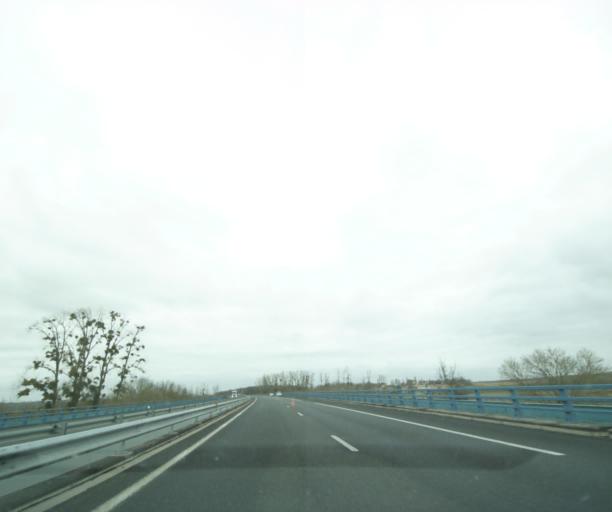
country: FR
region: Poitou-Charentes
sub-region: Departement de la Charente-Maritime
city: Saint-Savinien
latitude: 45.8803
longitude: -0.7367
